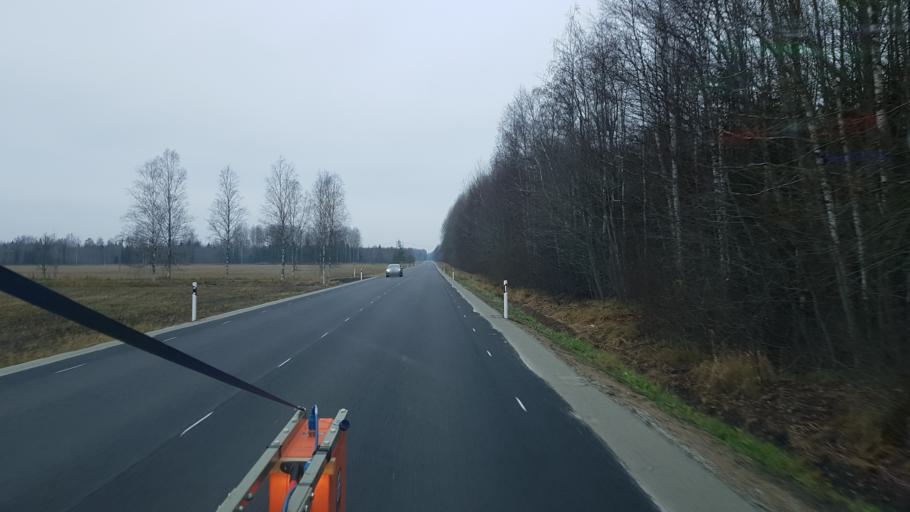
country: EE
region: Paernumaa
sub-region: Vaendra vald (alev)
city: Vandra
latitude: 58.8366
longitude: 25.0810
